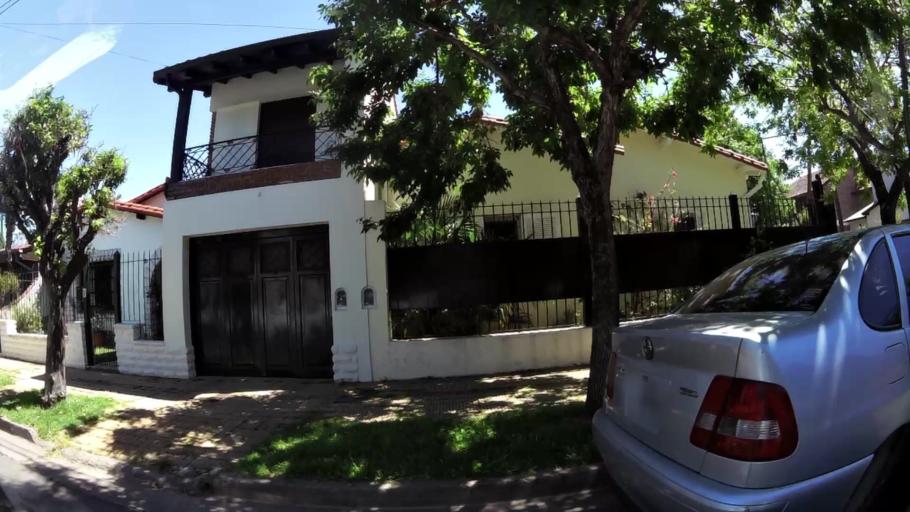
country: AR
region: Buenos Aires
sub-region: Partido de San Isidro
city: San Isidro
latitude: -34.4861
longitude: -58.5122
